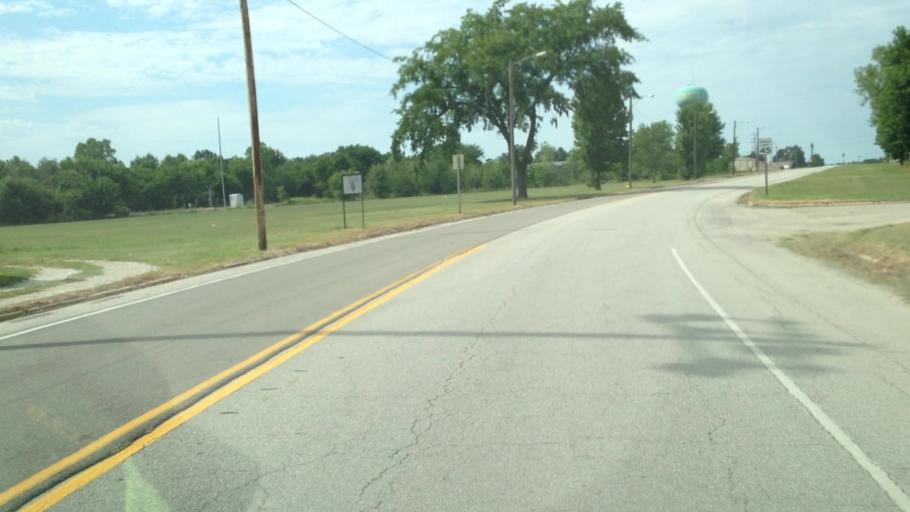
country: US
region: Kansas
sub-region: Labette County
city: Chetopa
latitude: 37.0387
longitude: -95.1001
